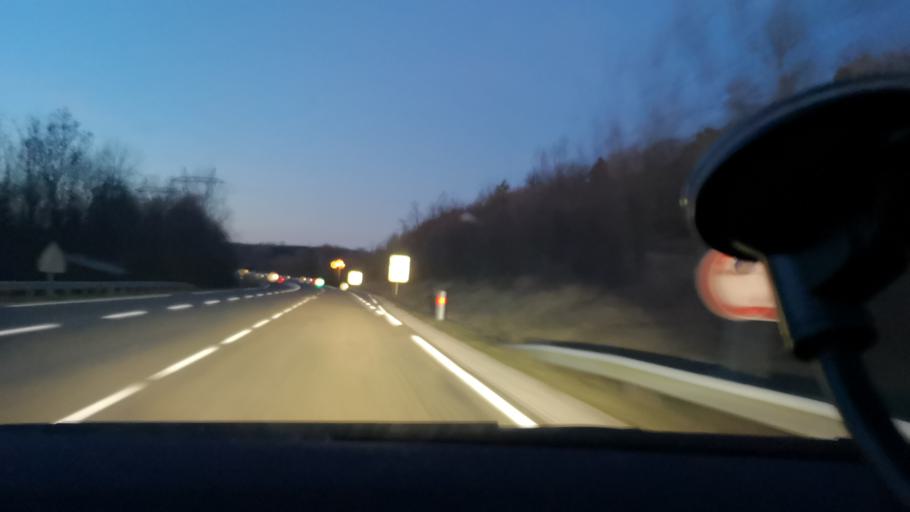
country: FR
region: Franche-Comte
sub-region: Departement du Jura
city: Champagnole
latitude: 46.7576
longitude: 5.9101
